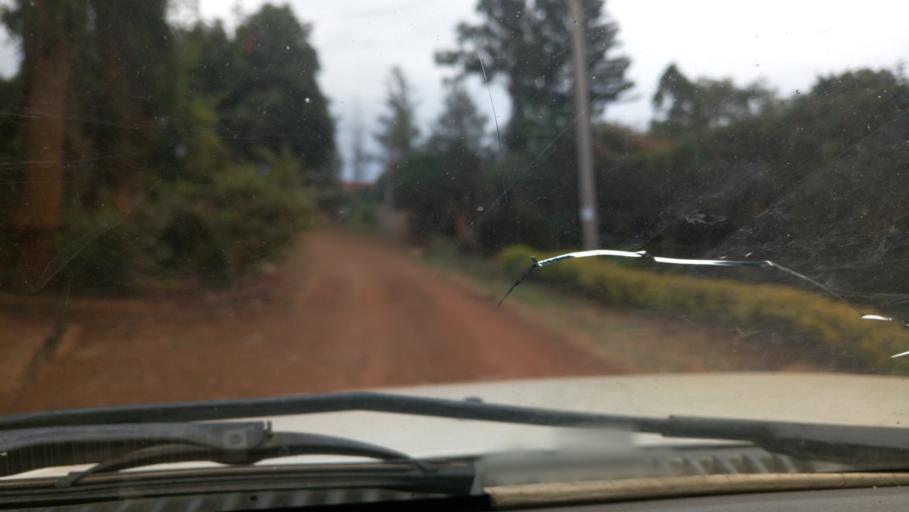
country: KE
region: Nairobi Area
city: Pumwani
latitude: -1.2302
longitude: 36.8746
